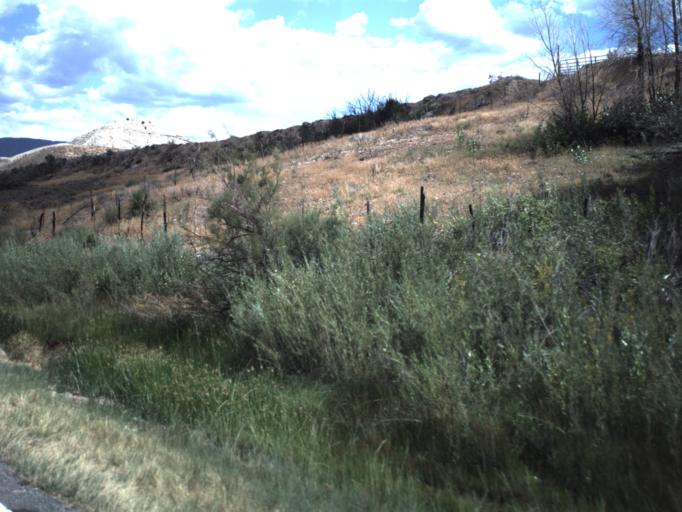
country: US
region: Utah
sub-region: Sanpete County
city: Gunnison
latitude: 39.1455
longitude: -111.7493
